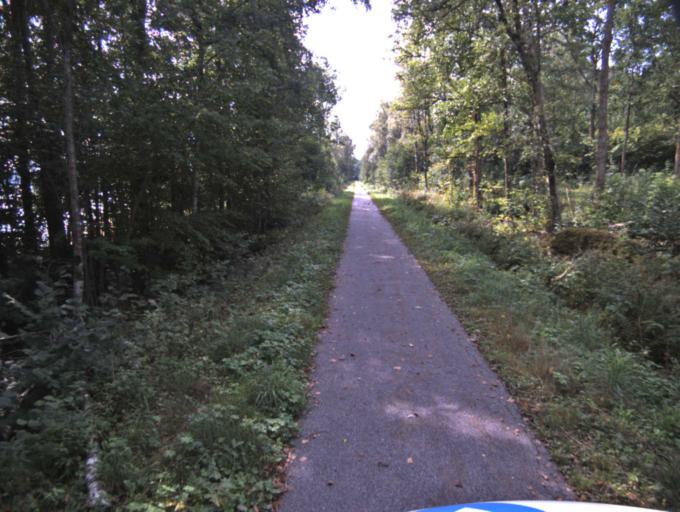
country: SE
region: Vaestra Goetaland
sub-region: Tranemo Kommun
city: Limmared
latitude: 57.6387
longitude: 13.3553
